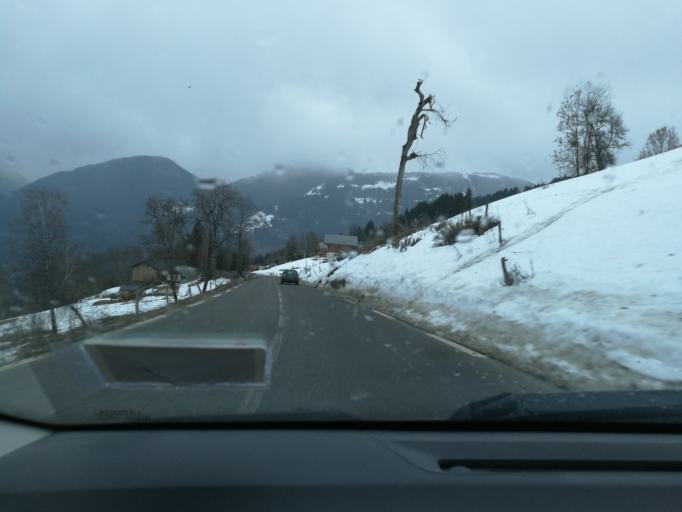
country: FR
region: Rhone-Alpes
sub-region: Departement de la Haute-Savoie
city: Passy
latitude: 45.8905
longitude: 6.6750
